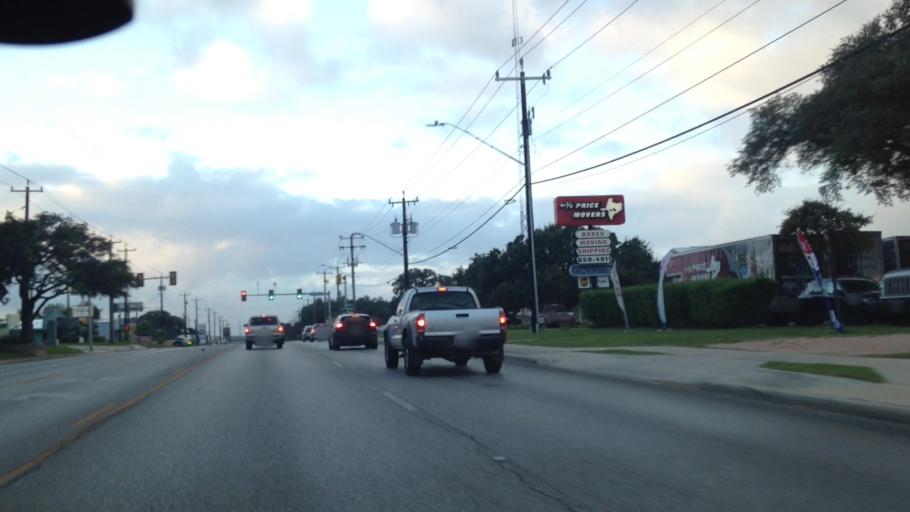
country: US
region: Texas
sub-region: Bexar County
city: Windcrest
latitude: 29.5409
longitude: -98.4111
